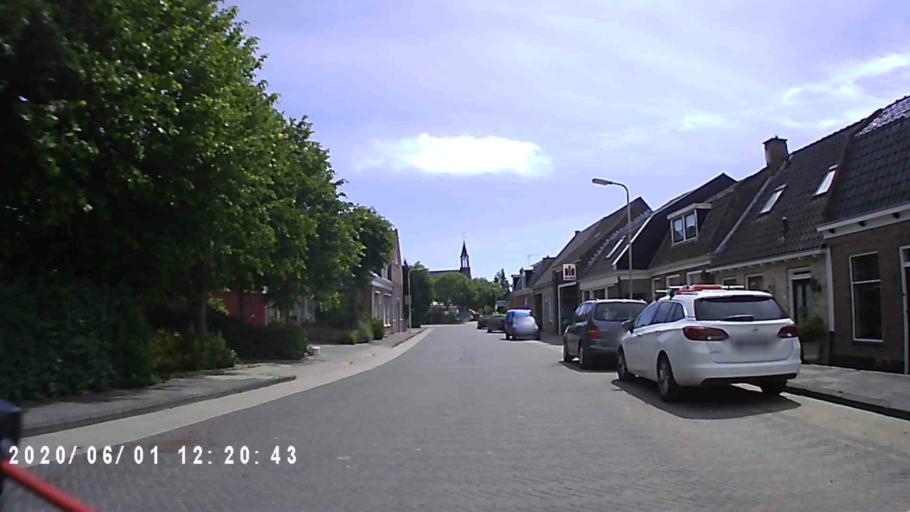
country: NL
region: Friesland
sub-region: Gemeente Harlingen
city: Harlingen
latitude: 53.1294
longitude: 5.4775
